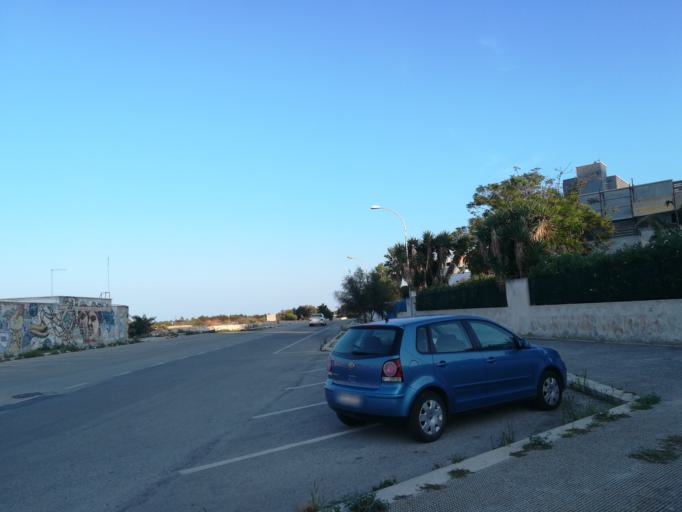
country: IT
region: Apulia
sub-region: Provincia di Bari
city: Polignano a Mare
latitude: 40.9915
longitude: 17.2307
